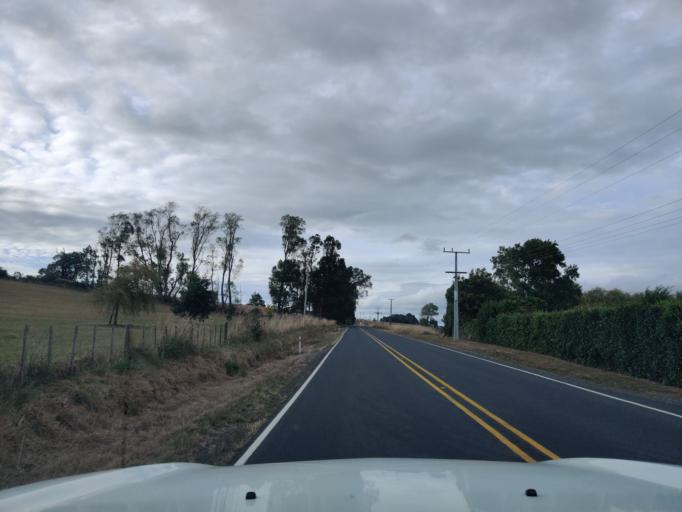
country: NZ
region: Waikato
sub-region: Waipa District
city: Cambridge
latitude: -37.8037
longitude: 175.4491
